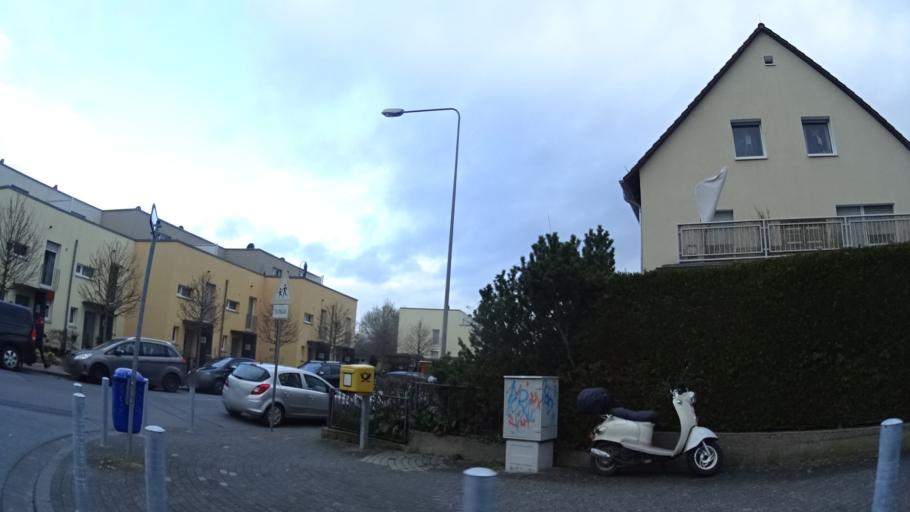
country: DE
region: Hesse
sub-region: Regierungsbezirk Darmstadt
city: Wiesbaden
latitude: 50.0601
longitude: 8.2623
